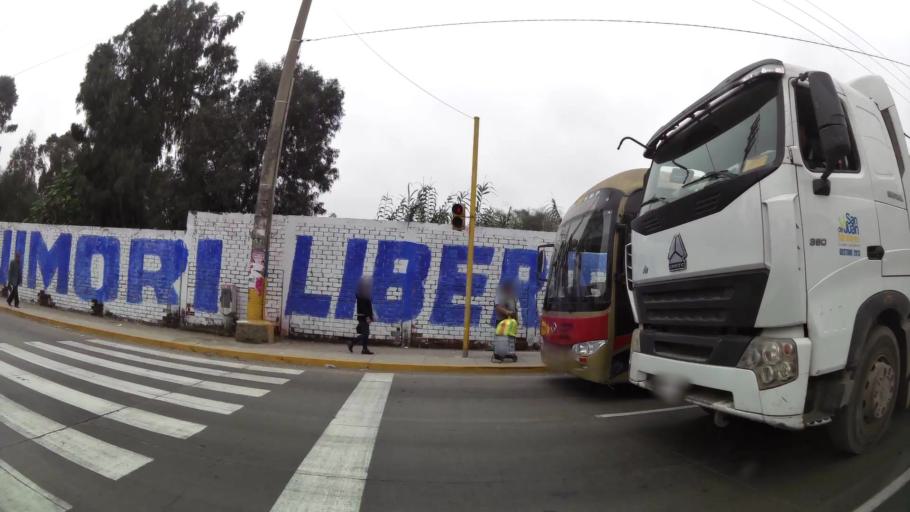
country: PE
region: Lima
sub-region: Lima
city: Surco
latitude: -12.1931
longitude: -76.9678
